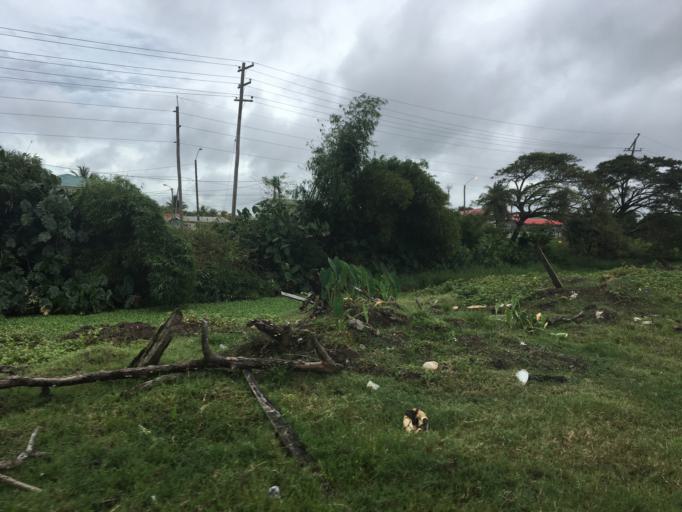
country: GY
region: Demerara-Mahaica
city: Georgetown
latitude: 6.8016
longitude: -58.1303
